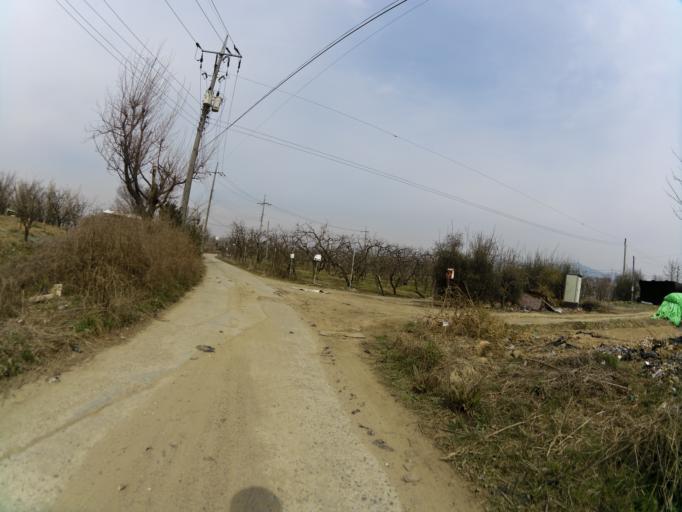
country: KR
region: Gyeongsangbuk-do
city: Gyeongsan-si
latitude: 35.8576
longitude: 128.7165
